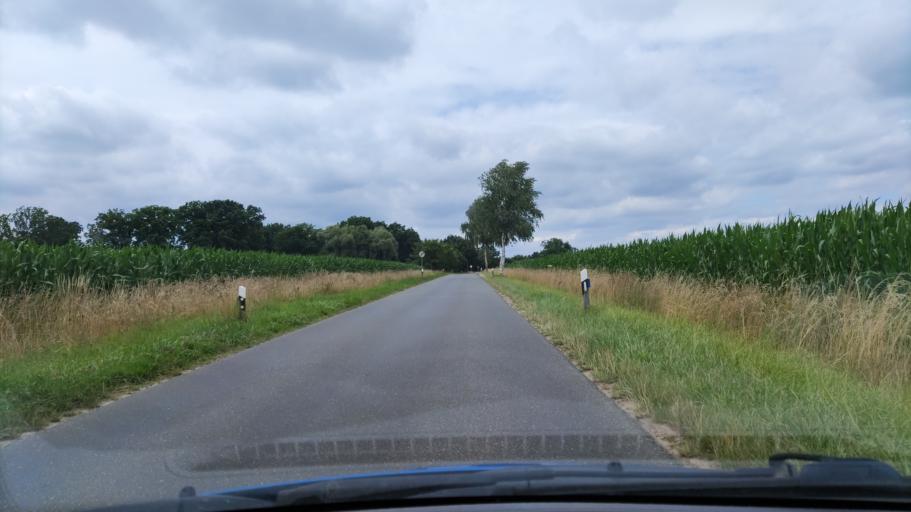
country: DE
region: Lower Saxony
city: Weste
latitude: 53.0674
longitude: 10.6947
